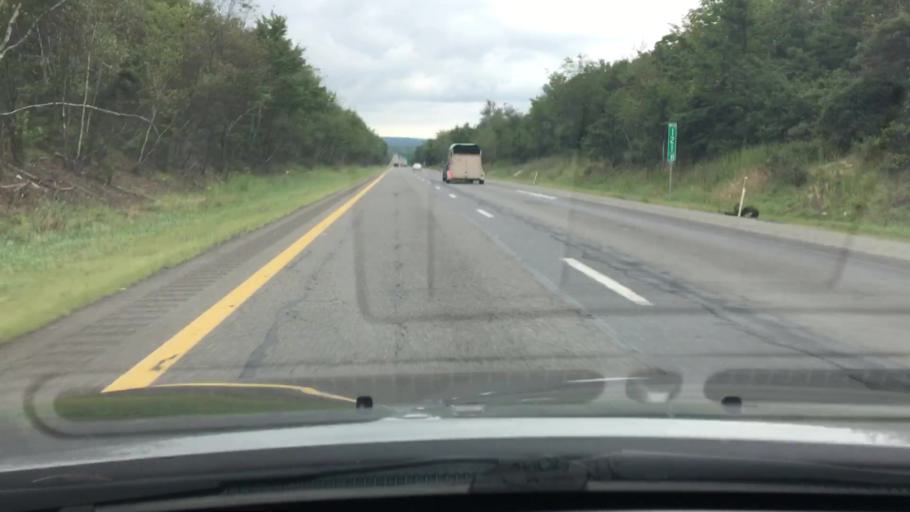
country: US
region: Pennsylvania
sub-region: Schuylkill County
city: Girardville
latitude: 40.7675
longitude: -76.2647
